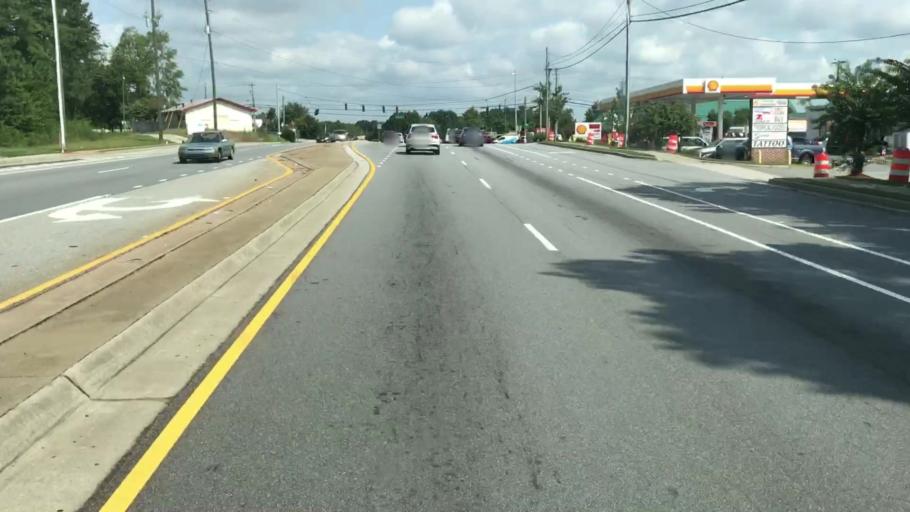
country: US
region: Georgia
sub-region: Gwinnett County
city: Lawrenceville
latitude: 33.9516
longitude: -84.0503
